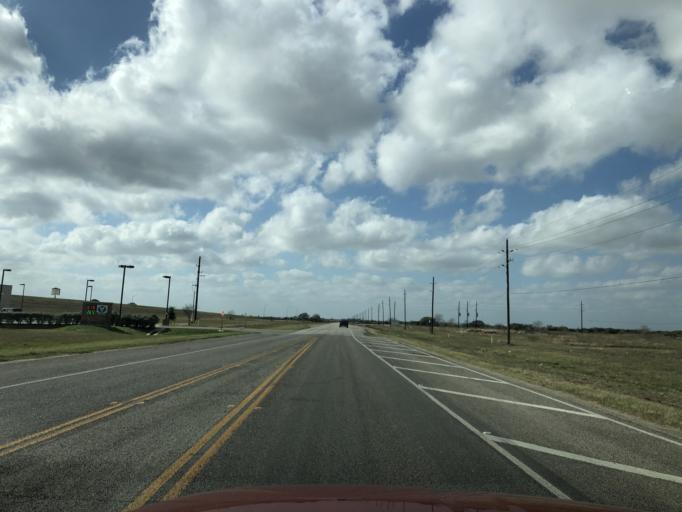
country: US
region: Texas
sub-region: Austin County
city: Sealy
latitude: 29.7648
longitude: -96.1849
